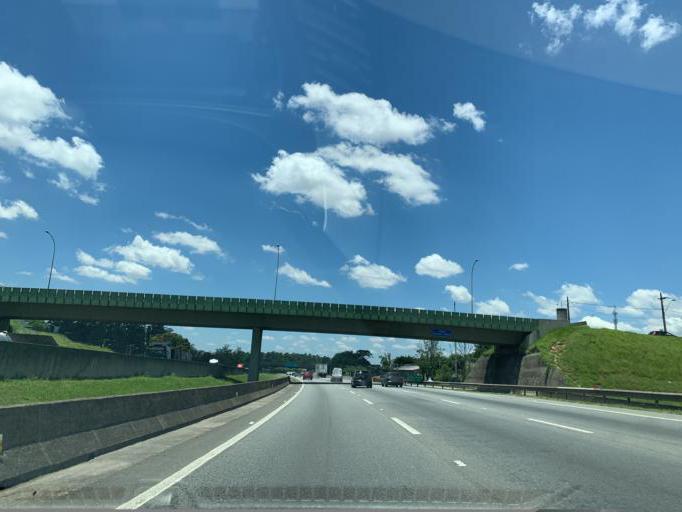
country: BR
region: Sao Paulo
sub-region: Itaquaquecetuba
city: Itaquaquecetuba
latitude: -23.4704
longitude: -46.4333
